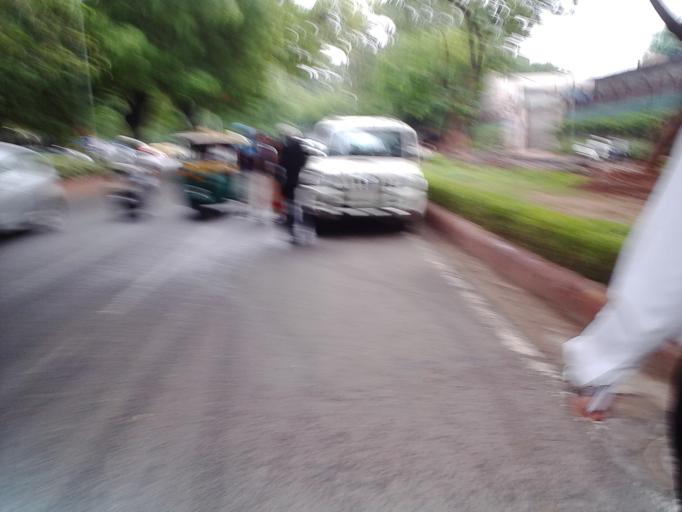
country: IN
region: NCT
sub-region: New Delhi
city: New Delhi
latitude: 28.6100
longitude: 77.2359
